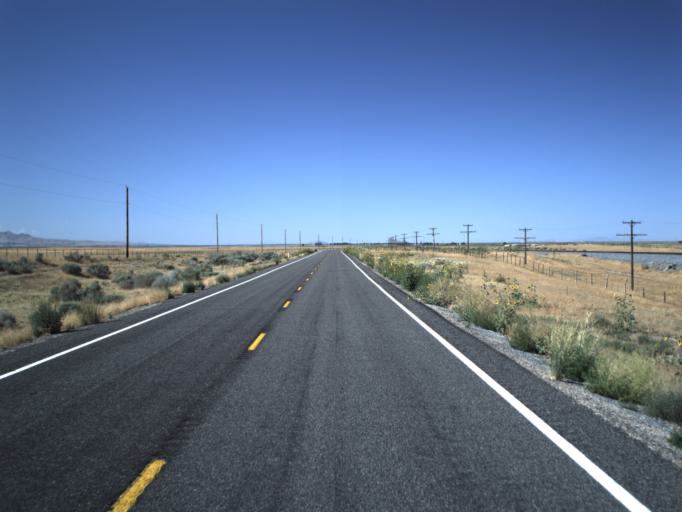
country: US
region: Utah
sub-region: Millard County
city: Delta
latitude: 39.5954
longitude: -112.3277
